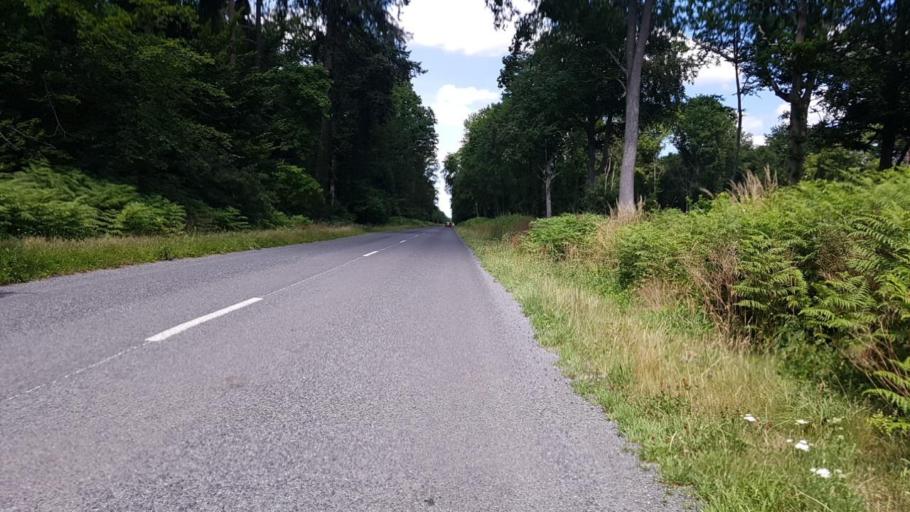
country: FR
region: Picardie
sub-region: Departement de l'Oise
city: Carlepont
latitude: 49.5116
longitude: 2.9833
